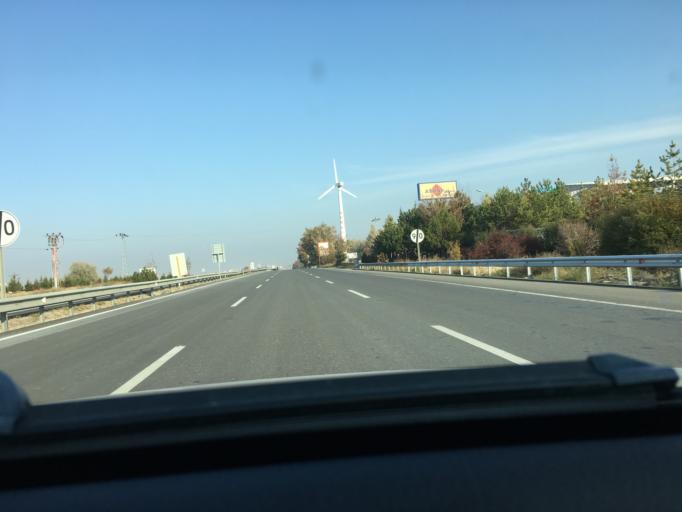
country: TR
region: Ankara
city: Temelli
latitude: 39.7143
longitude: 32.2989
